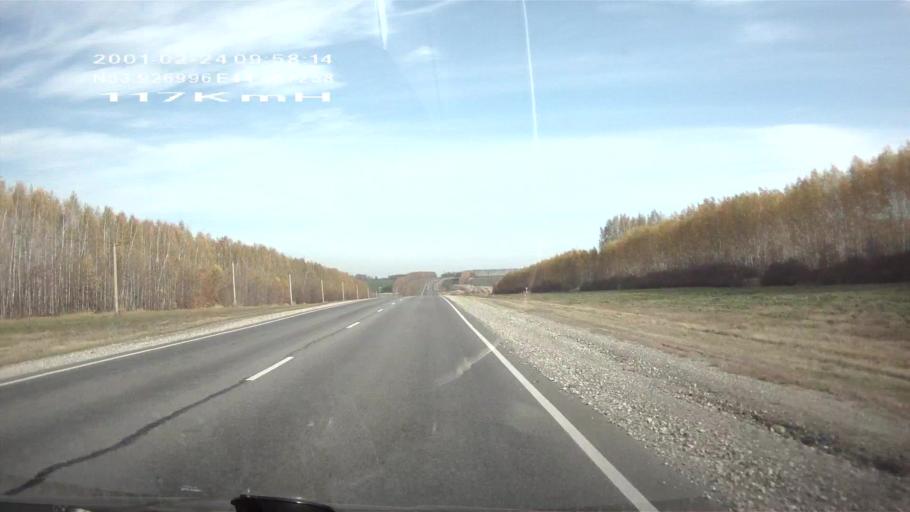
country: RU
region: Penza
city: Issa
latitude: 53.9274
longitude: 44.8676
